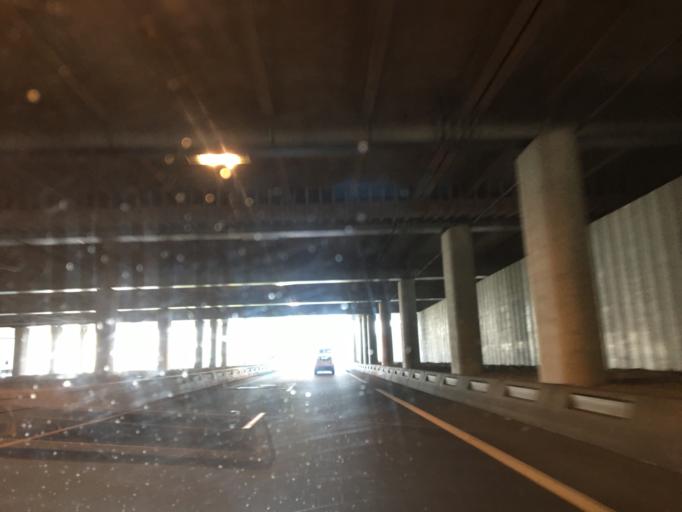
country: FR
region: Ile-de-France
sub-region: Departement de Seine-et-Marne
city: Mitry-Mory
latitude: 49.0048
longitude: 2.5900
